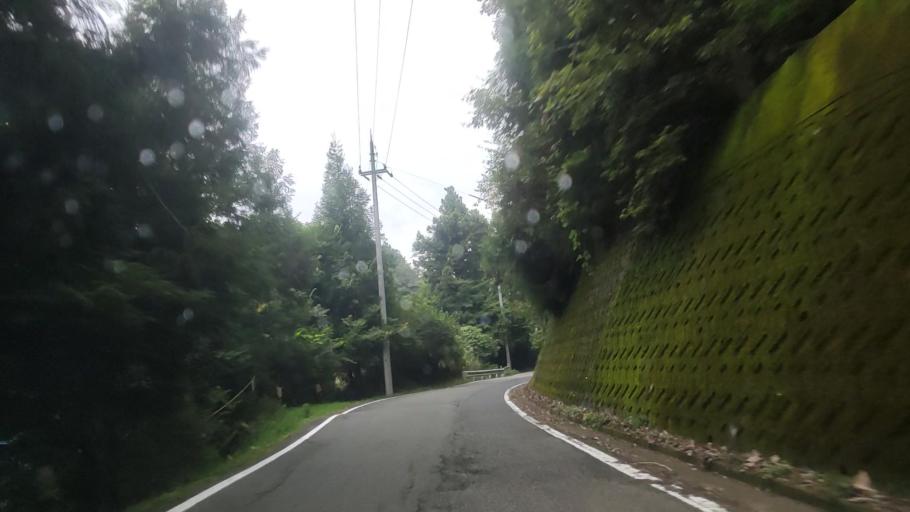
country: JP
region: Wakayama
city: Hashimoto
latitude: 34.2882
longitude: 135.6258
